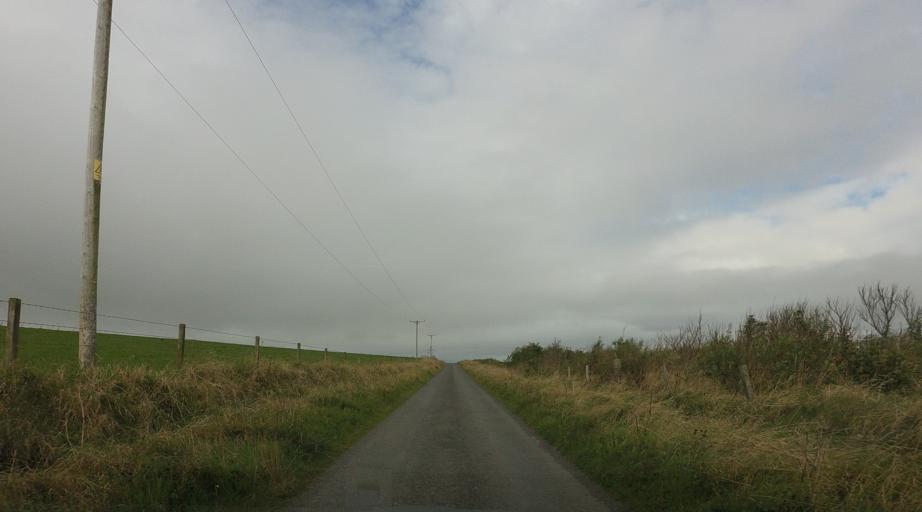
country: GB
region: Scotland
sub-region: Orkney Islands
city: Kirkwall
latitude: 58.8083
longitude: -2.9279
